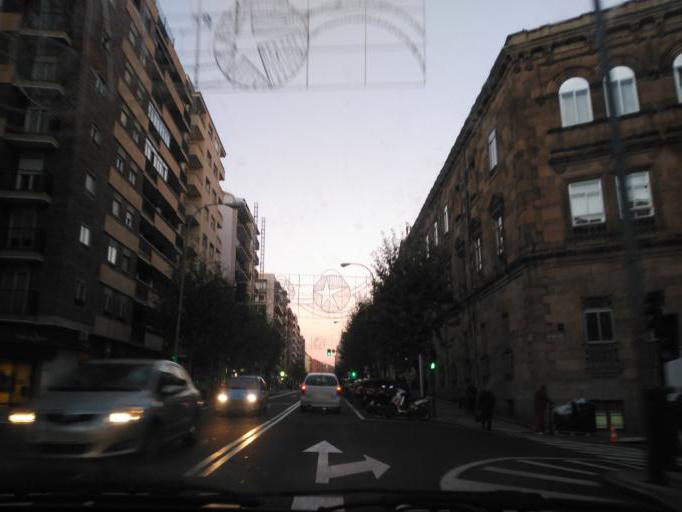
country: ES
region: Castille and Leon
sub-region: Provincia de Salamanca
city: Salamanca
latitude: 40.9699
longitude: -5.6586
